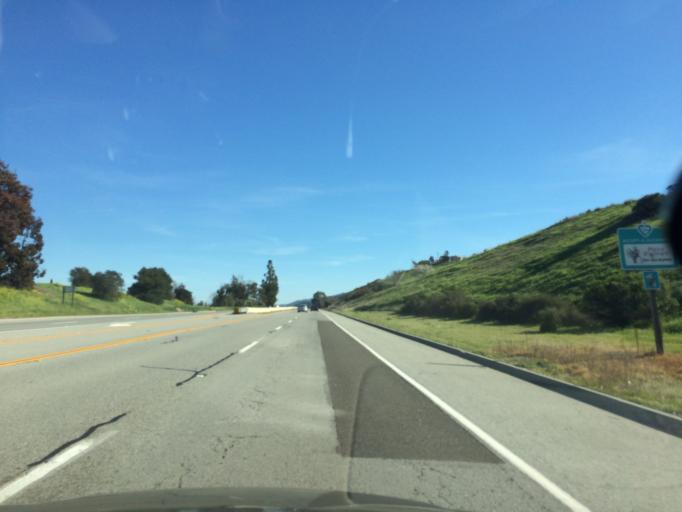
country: US
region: California
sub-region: San Benito County
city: San Juan Bautista
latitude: 36.8445
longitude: -121.5453
